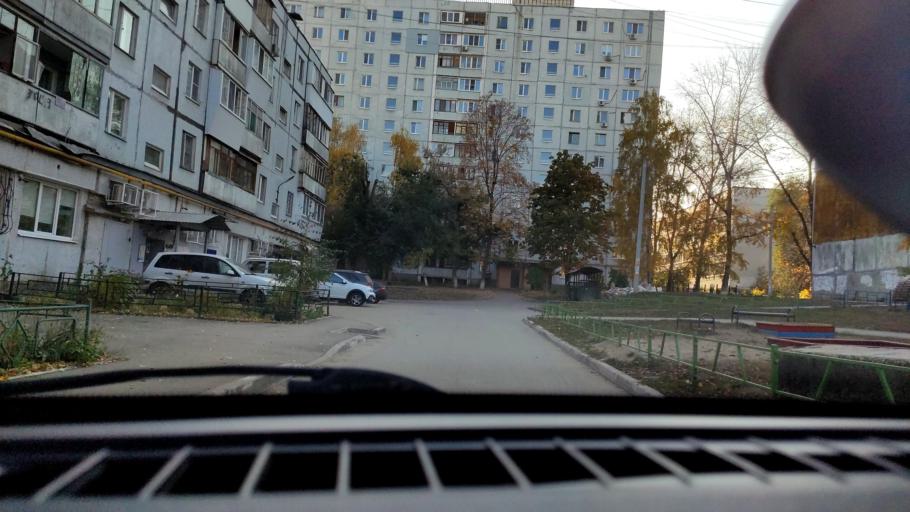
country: RU
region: Samara
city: Samara
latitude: 53.2491
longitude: 50.2561
